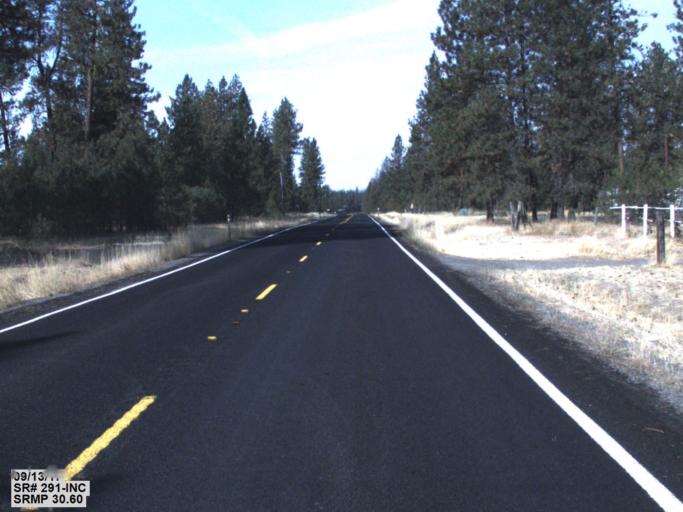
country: US
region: Washington
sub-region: Spokane County
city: Fairchild Air Force Base
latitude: 47.8392
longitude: -117.8083
